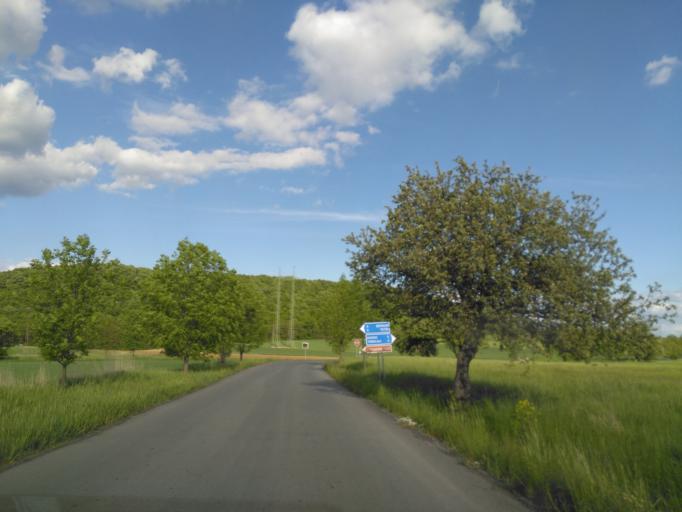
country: CZ
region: Central Bohemia
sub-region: Okres Beroun
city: Beroun
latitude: 49.9287
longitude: 14.0802
